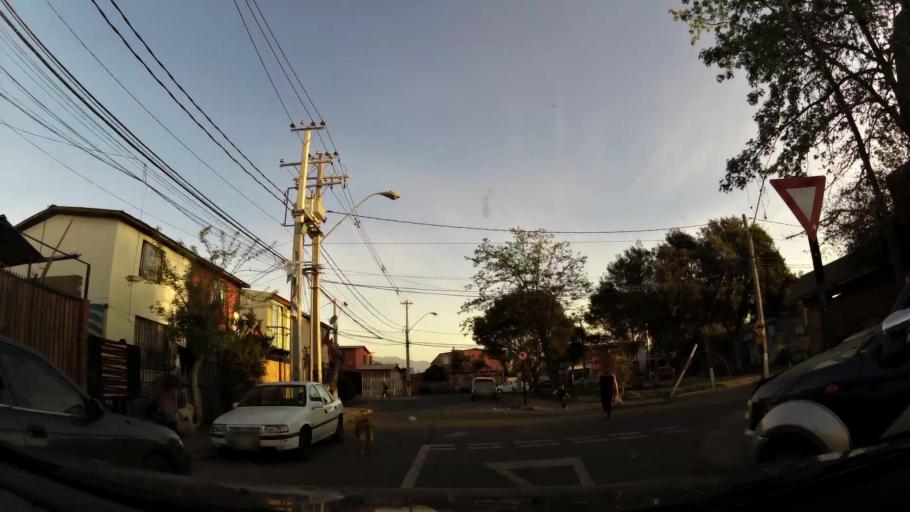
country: CL
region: Santiago Metropolitan
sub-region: Provincia de Cordillera
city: Puente Alto
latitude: -33.5992
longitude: -70.5688
